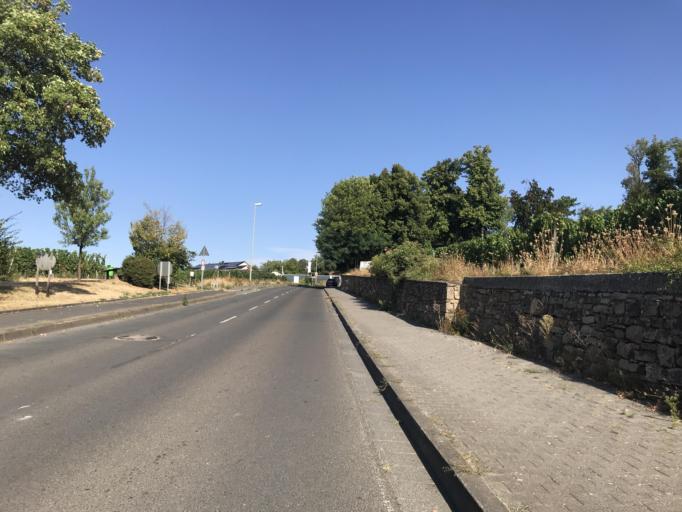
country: DE
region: Hesse
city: Geisenheim
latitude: 50.0071
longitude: 7.9778
